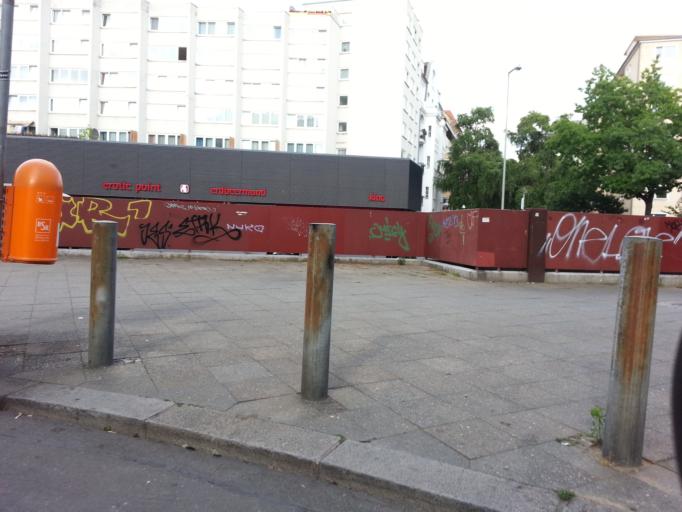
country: DE
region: Berlin
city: Halensee
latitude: 52.5022
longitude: 13.3050
